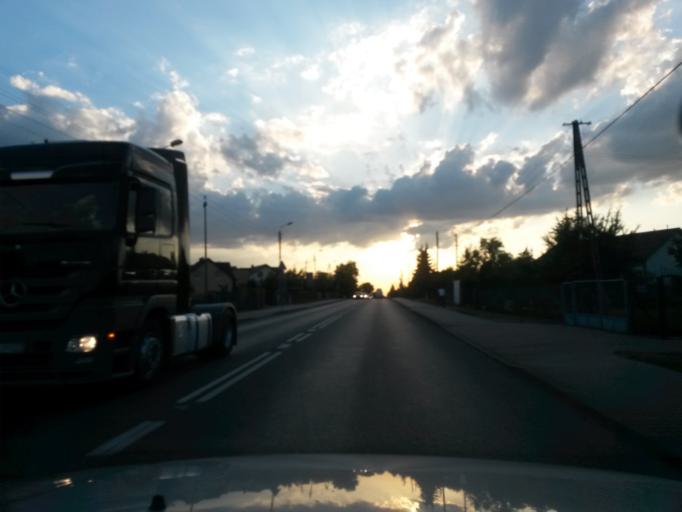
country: PL
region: Lodz Voivodeship
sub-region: Powiat wielunski
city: Wielun
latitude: 51.2288
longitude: 18.5500
